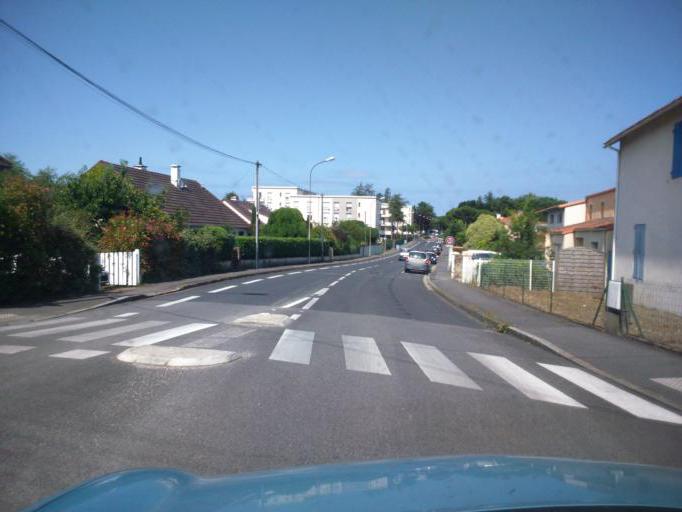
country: FR
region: Pays de la Loire
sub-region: Departement de la Loire-Atlantique
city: Saint-Sebastien-sur-Loire
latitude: 47.2025
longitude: -1.5229
